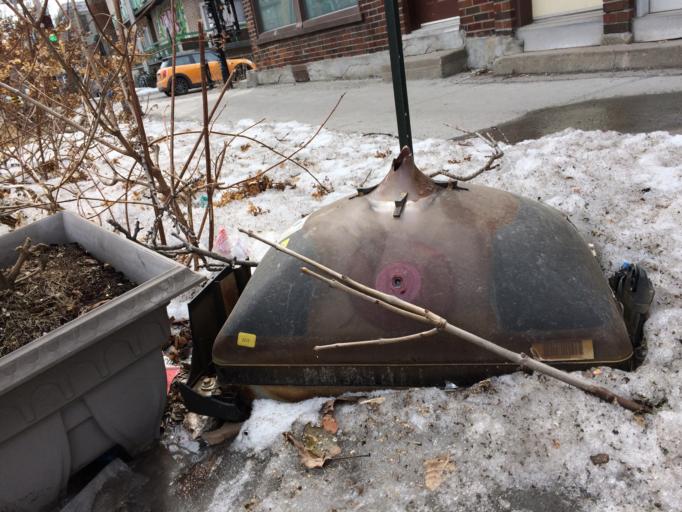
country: CA
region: Quebec
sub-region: Montreal
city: Montreal
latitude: 45.5278
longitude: -73.5765
